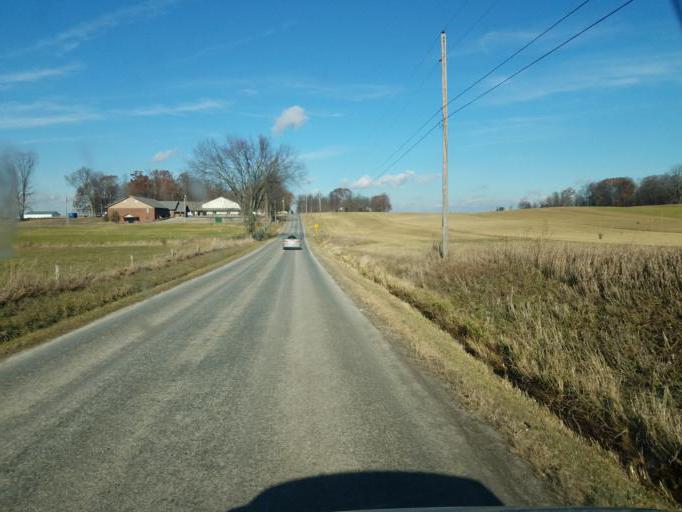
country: US
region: Ohio
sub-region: Wayne County
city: Apple Creek
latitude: 40.7433
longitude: -81.7752
